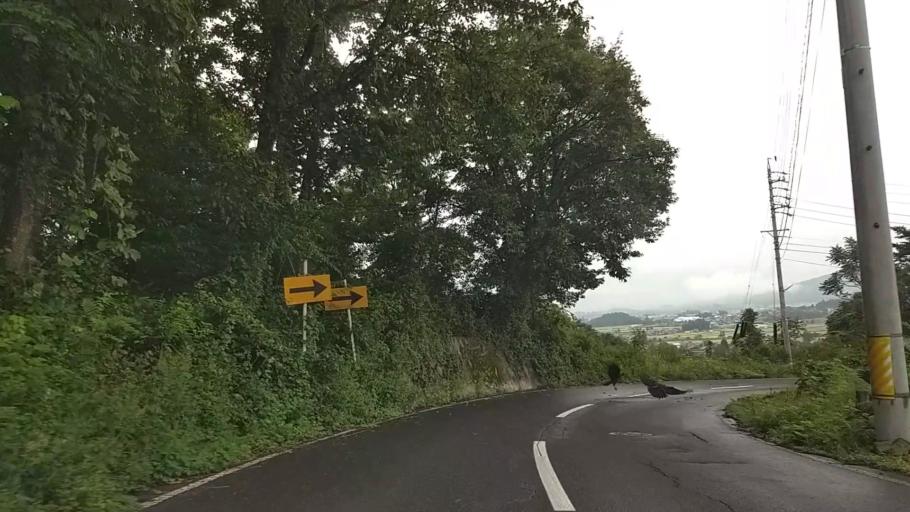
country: JP
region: Nagano
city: Iiyama
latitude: 36.8304
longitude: 138.4083
